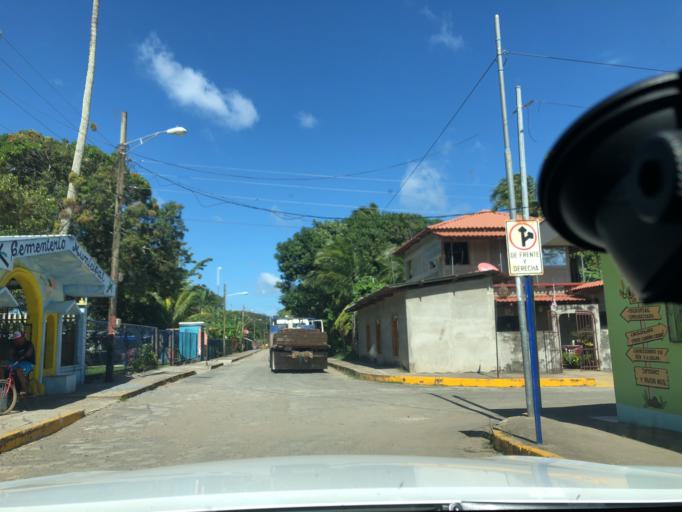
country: NI
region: Rivas
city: Cardenas
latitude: 11.1963
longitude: -85.5097
